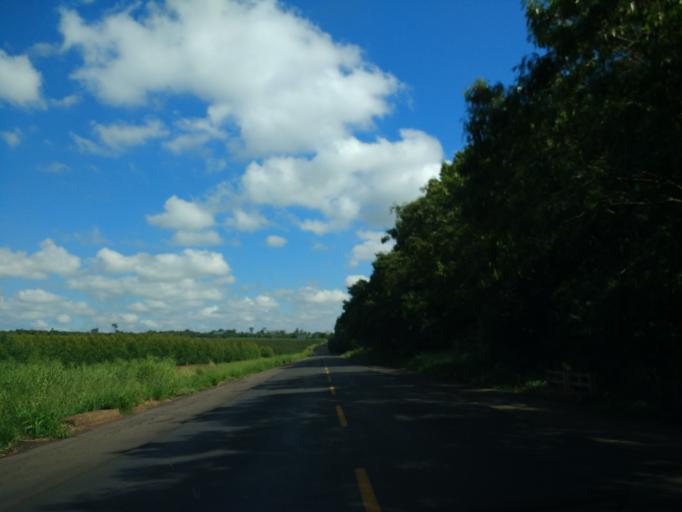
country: BR
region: Parana
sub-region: Umuarama
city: Umuarama
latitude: -23.8483
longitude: -53.3686
